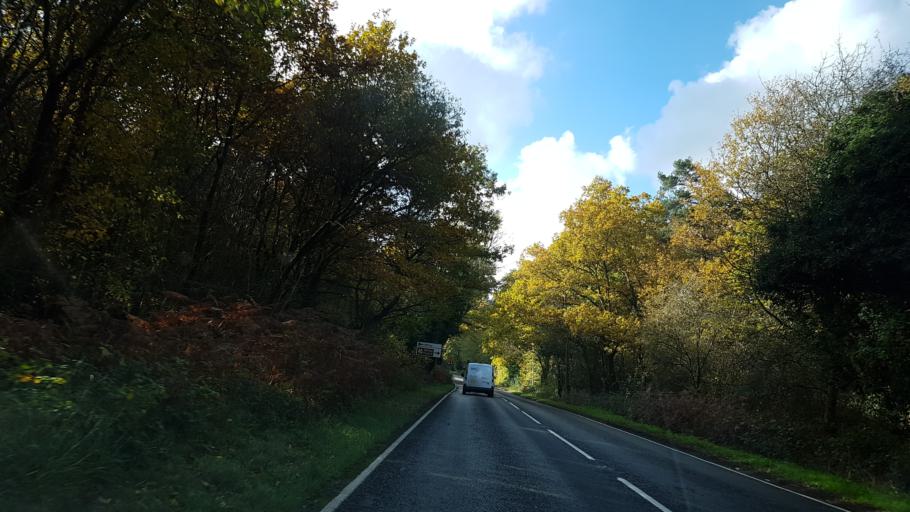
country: GB
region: England
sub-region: Surrey
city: Milford
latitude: 51.1600
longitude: -0.6620
